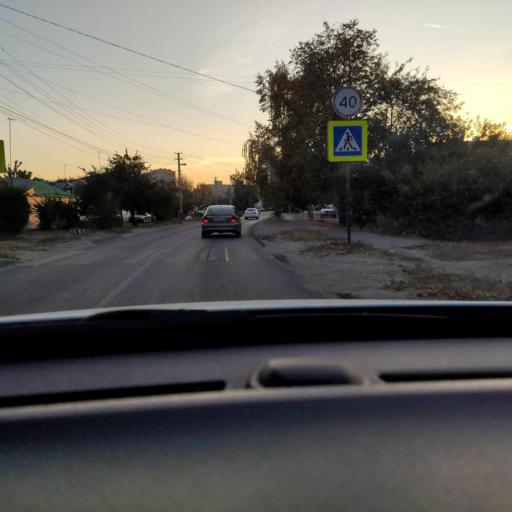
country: RU
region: Voronezj
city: Voronezh
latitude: 51.6987
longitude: 39.2657
